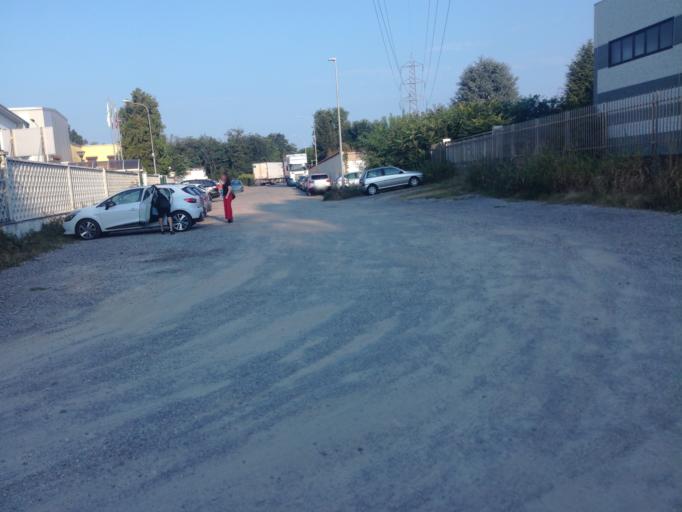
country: IT
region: Lombardy
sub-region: Provincia di Varese
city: Cascina Elisa
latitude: 45.5946
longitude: 8.7953
